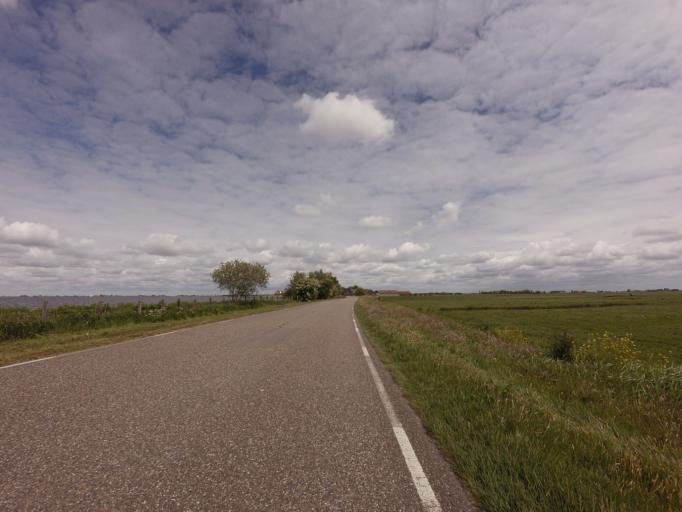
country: NL
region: Friesland
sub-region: Gemeente Gaasterlan-Sleat
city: Balk
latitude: 52.9343
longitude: 5.5528
